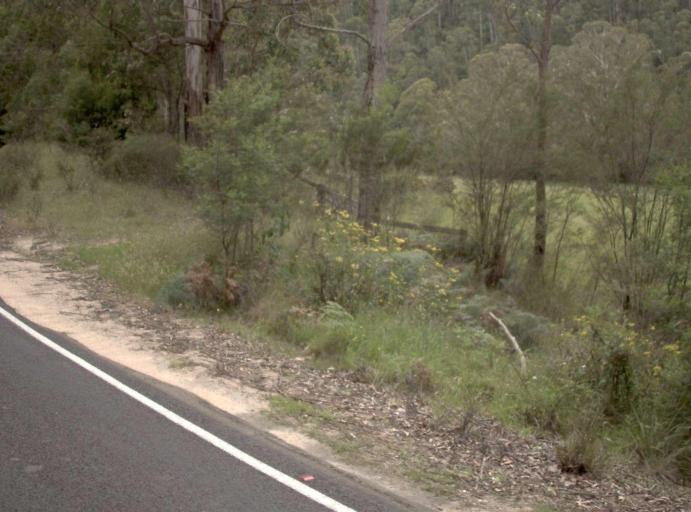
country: AU
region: New South Wales
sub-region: Bombala
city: Bombala
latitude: -37.4077
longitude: 149.1987
